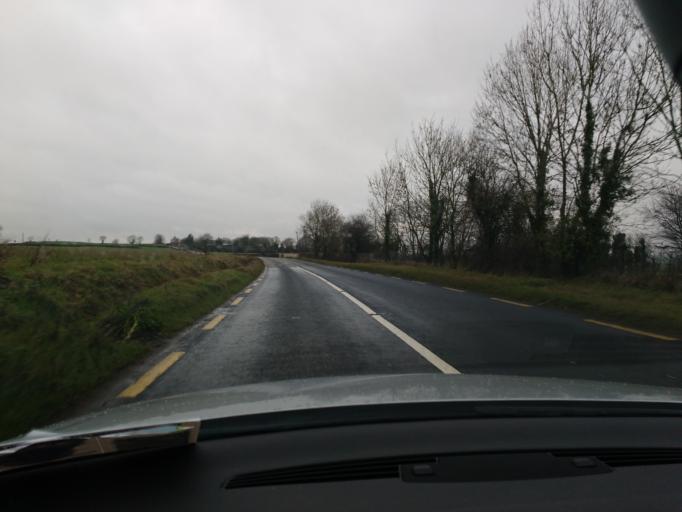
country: IE
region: Munster
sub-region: North Tipperary
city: Nenagh
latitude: 52.8408
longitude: -8.1380
